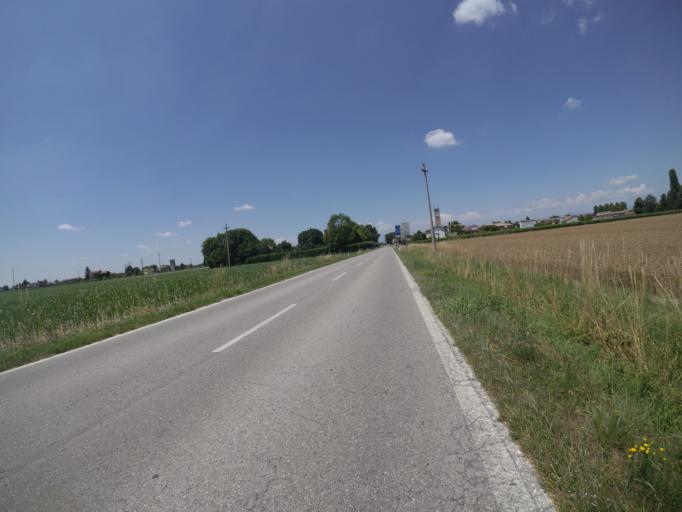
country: IT
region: Friuli Venezia Giulia
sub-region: Provincia di Udine
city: Varmo
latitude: 45.9061
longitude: 13.0064
